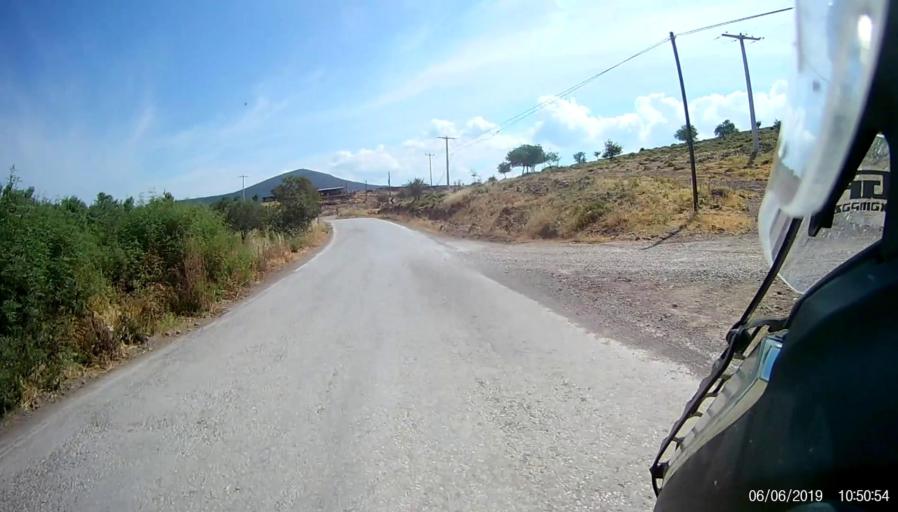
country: TR
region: Canakkale
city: Ayvacik
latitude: 39.5186
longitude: 26.4468
